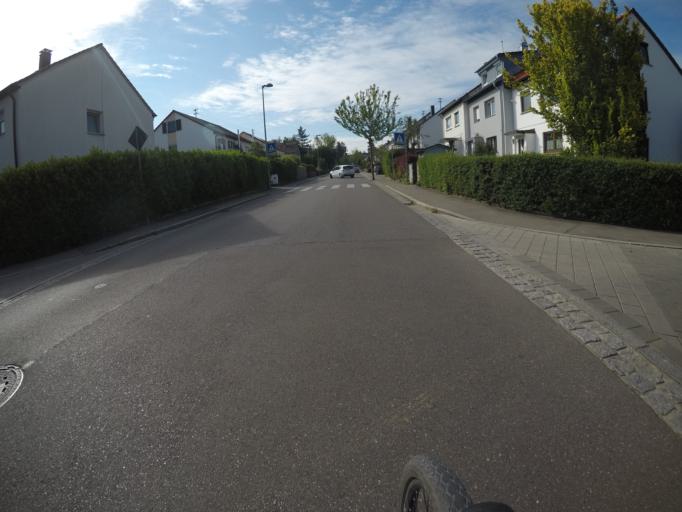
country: DE
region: Baden-Wuerttemberg
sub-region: Regierungsbezirk Stuttgart
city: Neuhausen auf den Fildern
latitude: 48.6794
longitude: 9.2756
